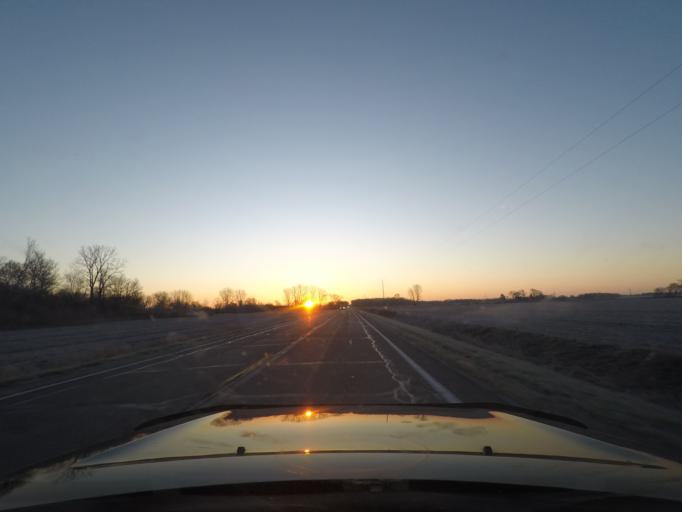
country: US
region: Indiana
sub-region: Saint Joseph County
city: Walkerton
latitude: 41.4763
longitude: -86.5619
